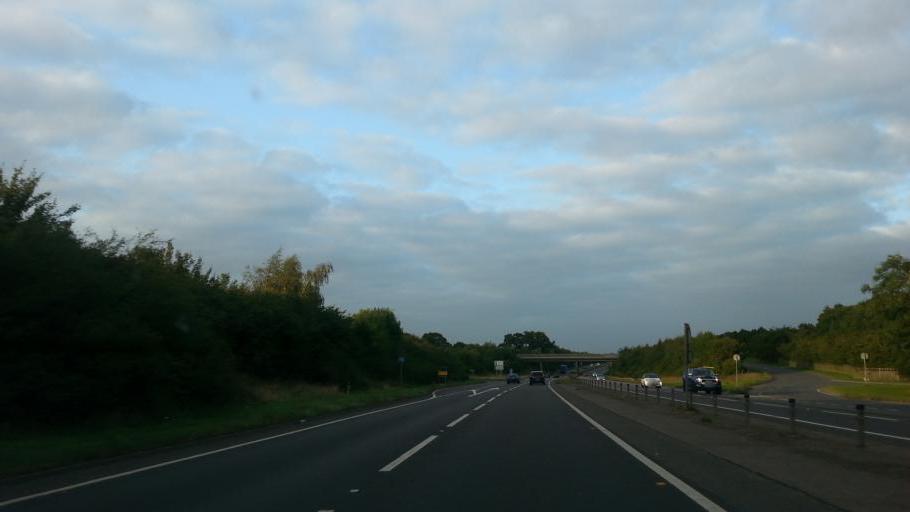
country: GB
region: England
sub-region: Northamptonshire
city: Brackley
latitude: 51.9715
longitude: -1.1928
